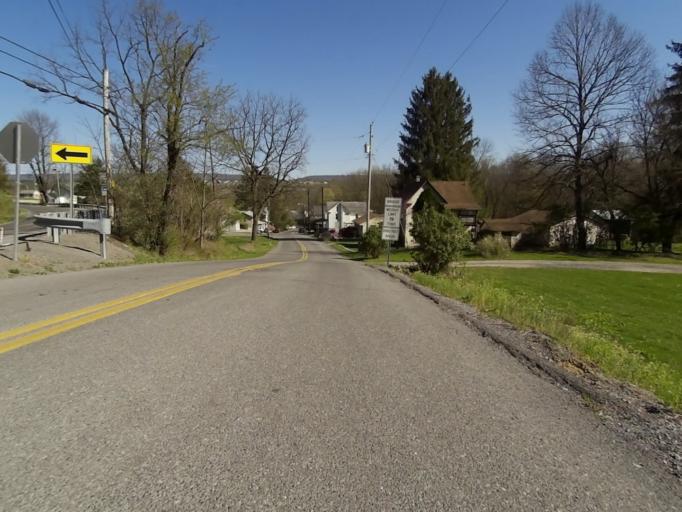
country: US
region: Pennsylvania
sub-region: Centre County
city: Bellefonte
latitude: 40.9098
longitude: -77.8005
